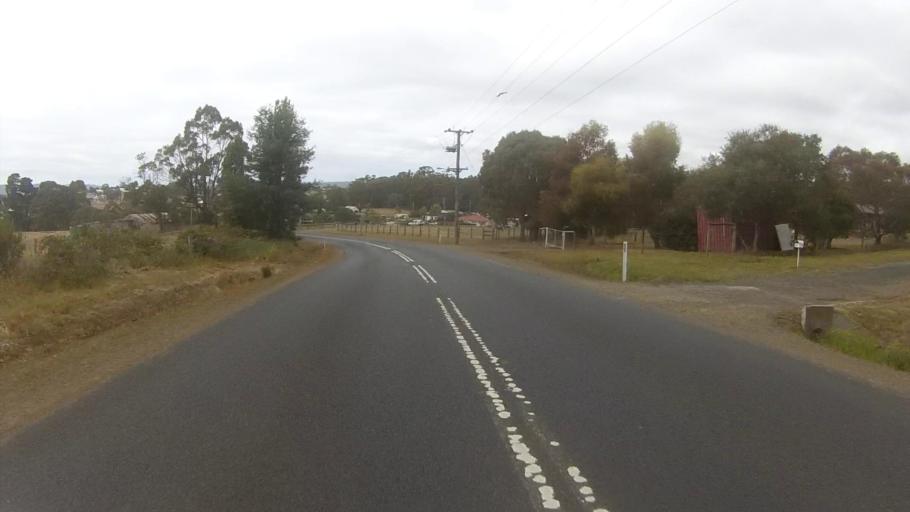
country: AU
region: Tasmania
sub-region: Kingborough
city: Margate
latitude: -43.0199
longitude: 147.2536
